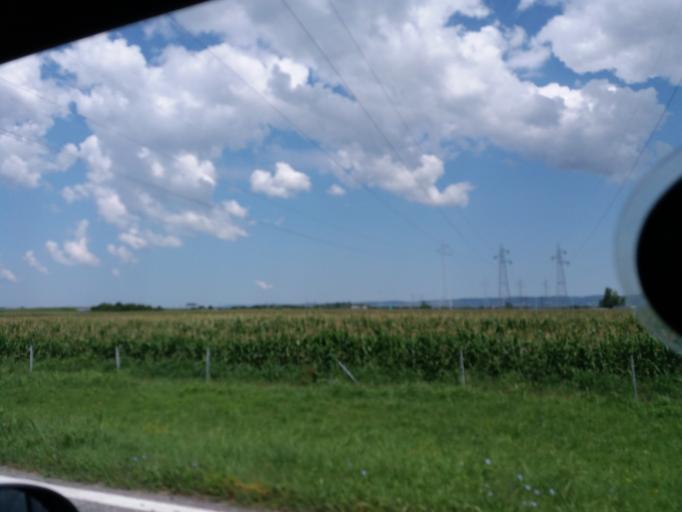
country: RS
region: Autonomna Pokrajina Vojvodina
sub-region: Sremski Okrug
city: Sremska Mitrovica
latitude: 44.9956
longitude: 19.6484
